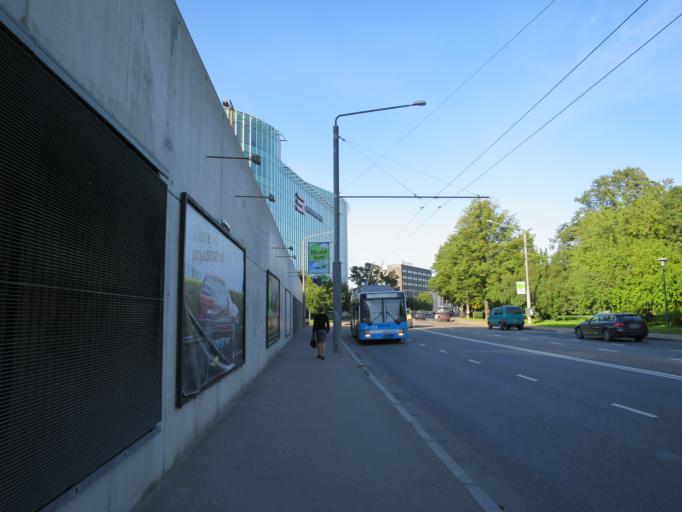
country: EE
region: Harju
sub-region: Tallinna linn
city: Tallinn
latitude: 59.4377
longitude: 24.7338
